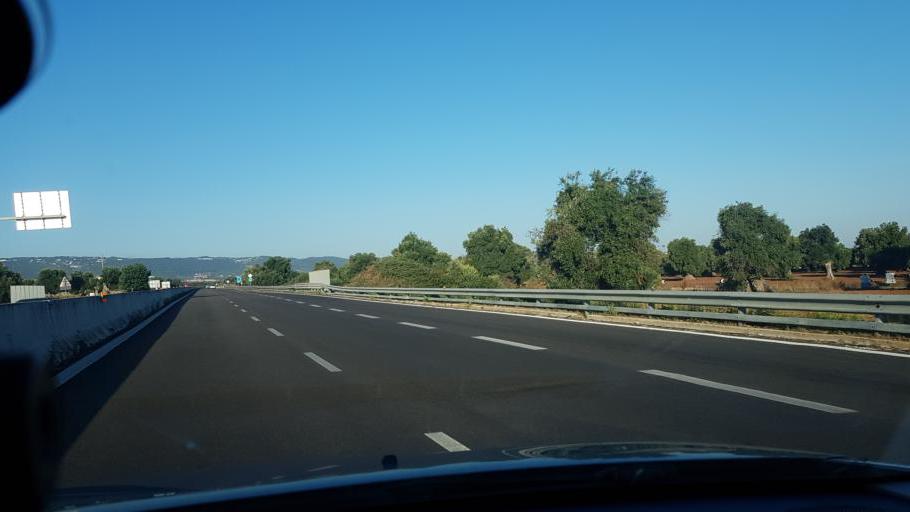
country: IT
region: Apulia
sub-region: Provincia di Brindisi
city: Pezze di Greco
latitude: 40.8339
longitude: 17.4058
